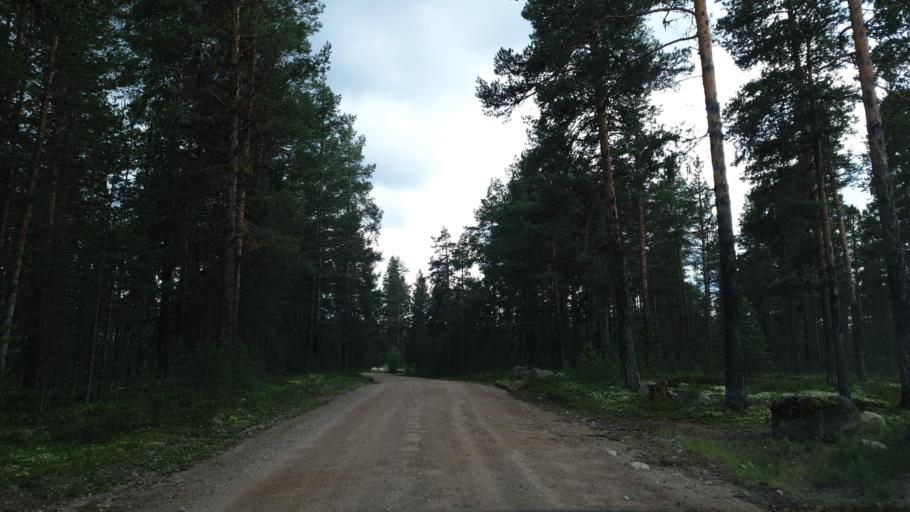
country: SE
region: Jaemtland
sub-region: Harjedalens Kommun
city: Sveg
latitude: 62.0268
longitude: 14.4716
